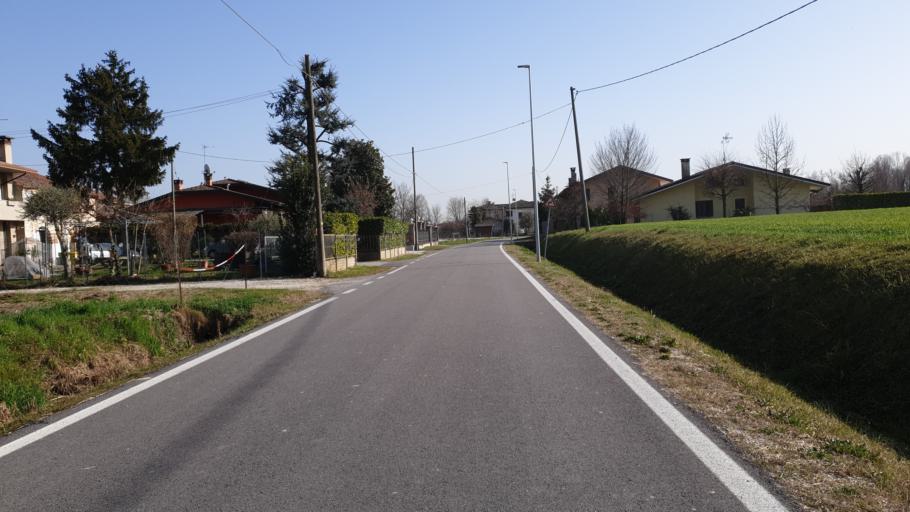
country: IT
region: Veneto
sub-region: Provincia di Padova
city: Saletto
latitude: 45.4809
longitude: 11.8796
